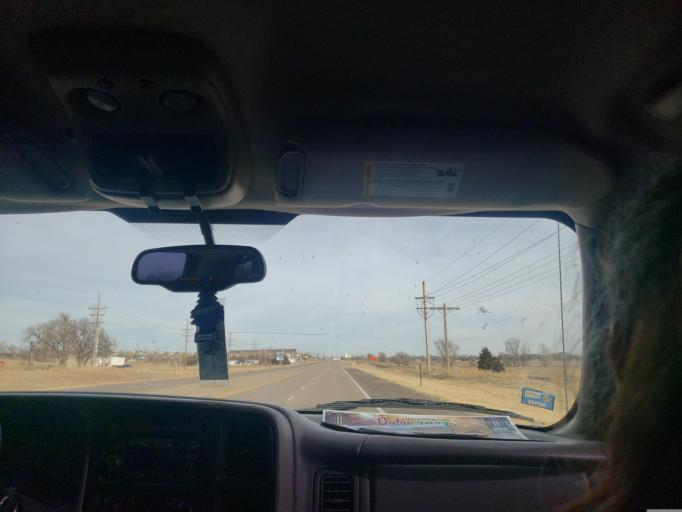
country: US
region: Kansas
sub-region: Ford County
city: Dodge City
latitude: 37.7550
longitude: -100.0649
